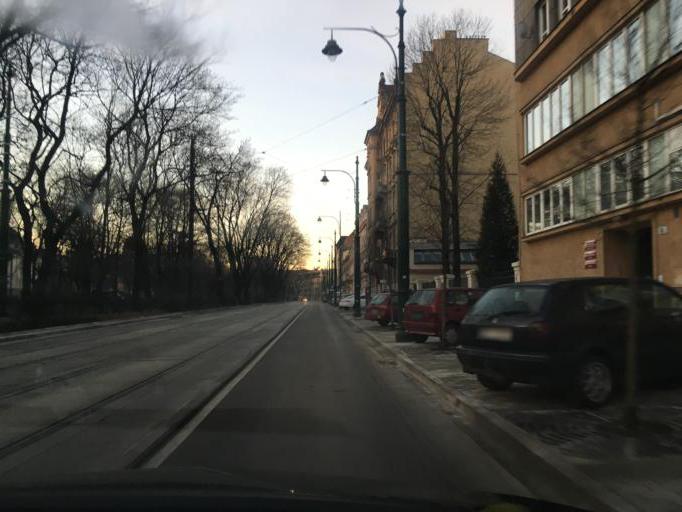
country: PL
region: Lesser Poland Voivodeship
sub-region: Krakow
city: Krakow
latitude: 50.0654
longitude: 19.9352
